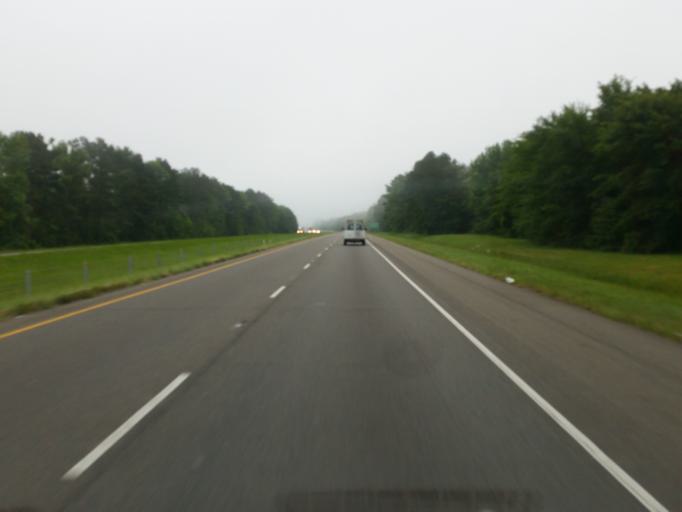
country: US
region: Louisiana
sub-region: Bossier Parish
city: Haughton
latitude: 32.5769
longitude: -93.4577
